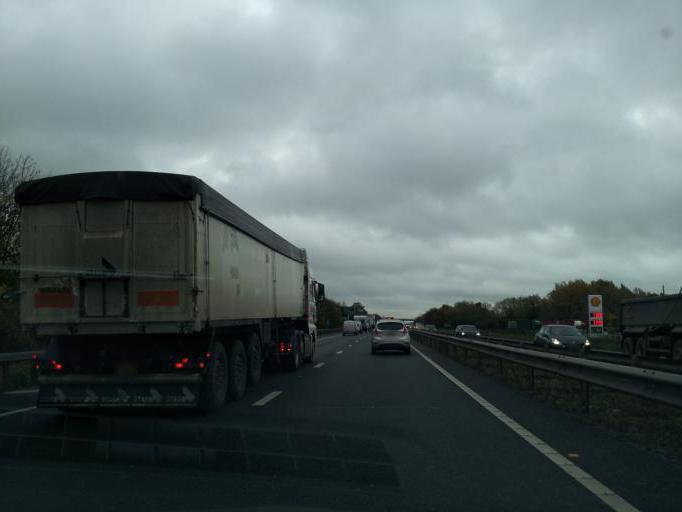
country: GB
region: England
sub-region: Oxfordshire
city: Kidlington
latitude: 51.8519
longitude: -1.2259
